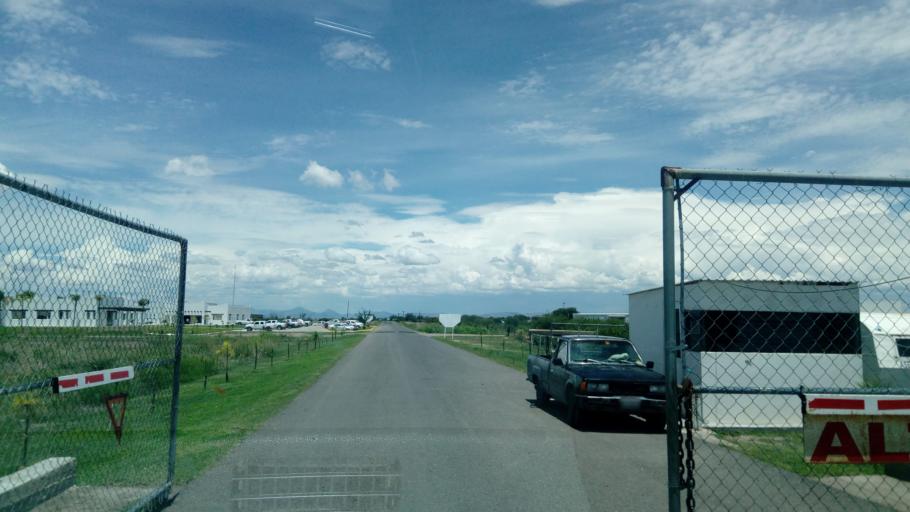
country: MX
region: Durango
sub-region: Durango
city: Jose Refugio Salcido
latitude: 24.1640
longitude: -104.5023
